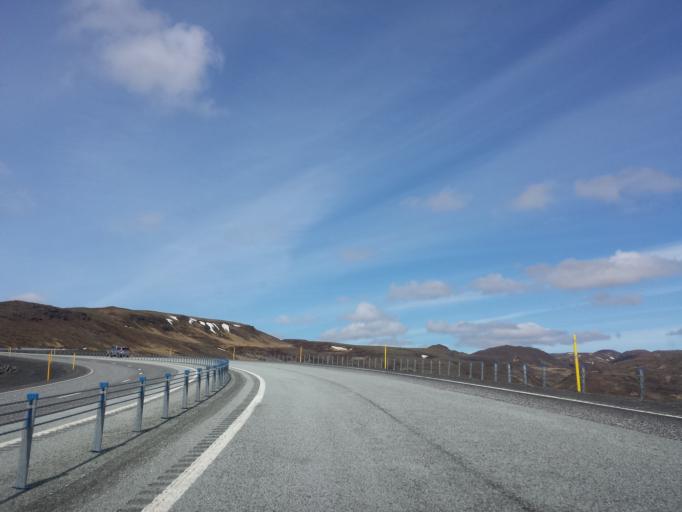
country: IS
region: South
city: Hveragerdi
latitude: 64.0129
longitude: -21.2221
